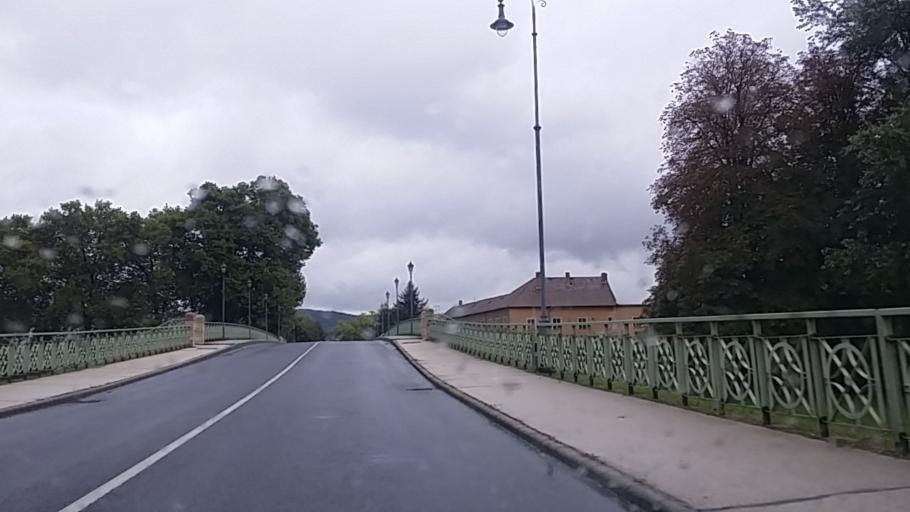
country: HU
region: Komarom-Esztergom
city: Esztergom
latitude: 47.7882
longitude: 18.7336
